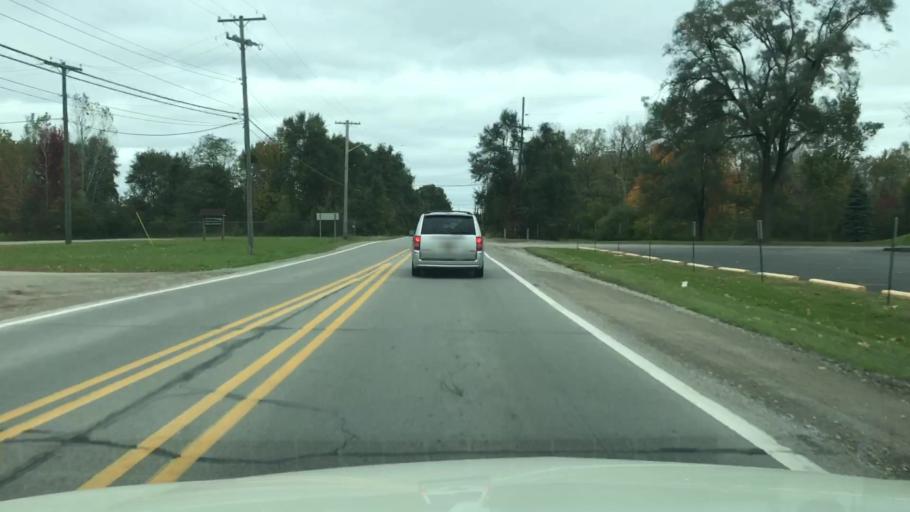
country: US
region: Michigan
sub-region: Macomb County
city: Shelby
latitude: 42.6619
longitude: -83.0734
